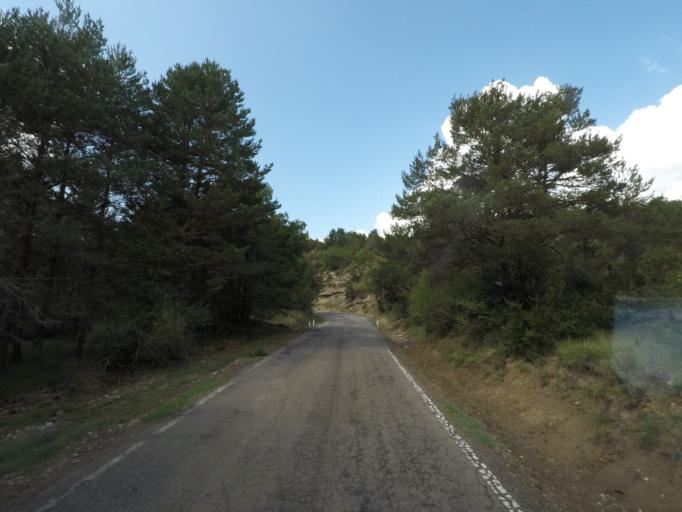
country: ES
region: Aragon
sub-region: Provincia de Huesca
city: Yebra de Basa
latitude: 42.3907
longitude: -0.3140
